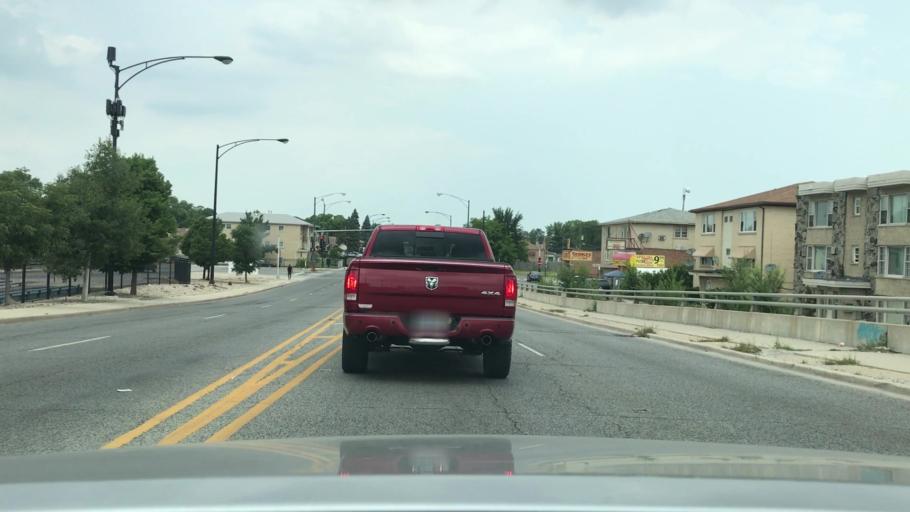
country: US
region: Illinois
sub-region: Cook County
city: Hometown
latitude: 41.7596
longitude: -87.7027
